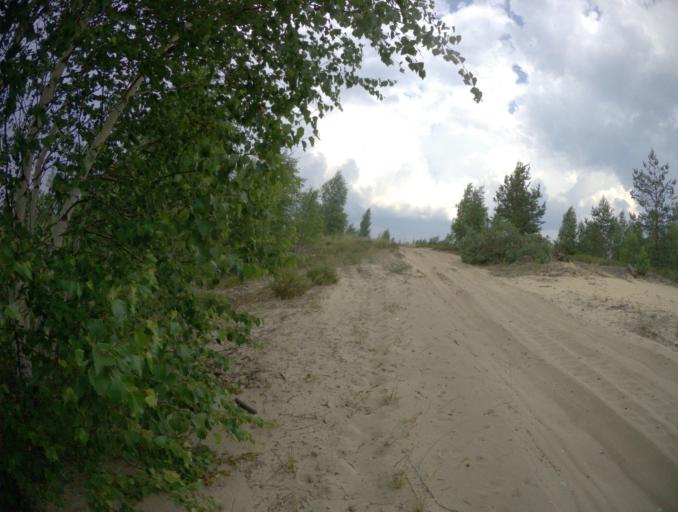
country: RU
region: Ivanovo
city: Talitsy
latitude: 56.4262
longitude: 42.3329
